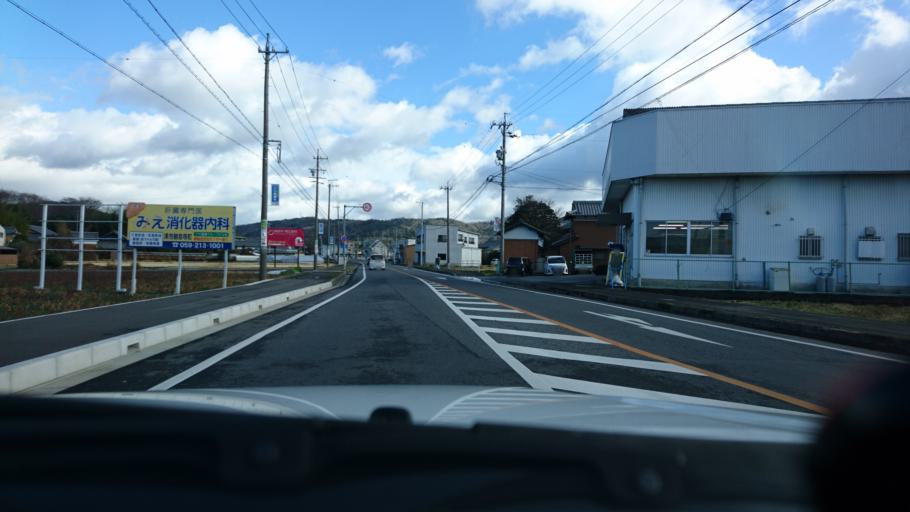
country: JP
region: Mie
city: Ueno-ebisumachi
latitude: 34.7712
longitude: 136.1502
